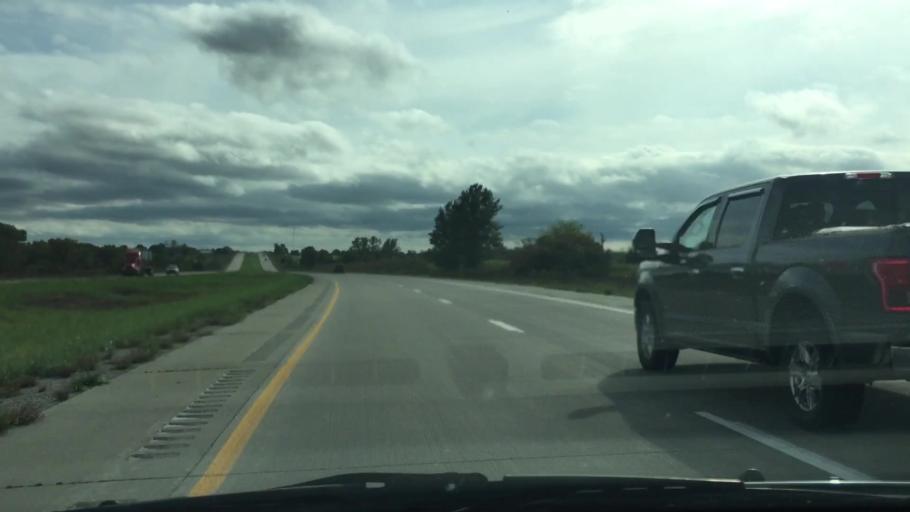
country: US
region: Iowa
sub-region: Decatur County
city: Leon
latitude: 40.7952
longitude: -93.8345
